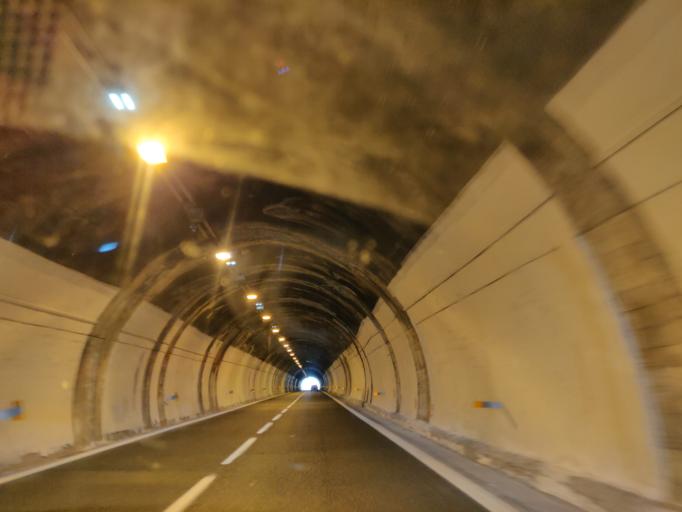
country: IT
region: Latium
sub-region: Citta metropolitana di Roma Capitale
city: Santa Marinella
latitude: 42.0432
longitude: 11.8624
